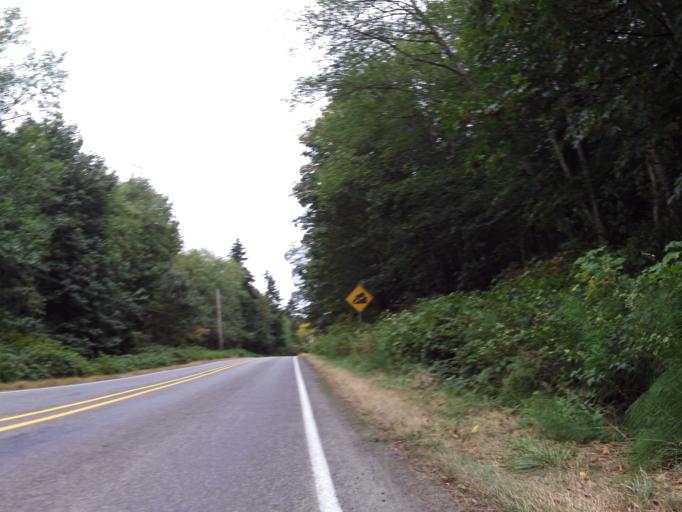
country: US
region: Washington
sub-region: Kitsap County
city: Lofall
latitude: 47.8726
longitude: -122.6362
